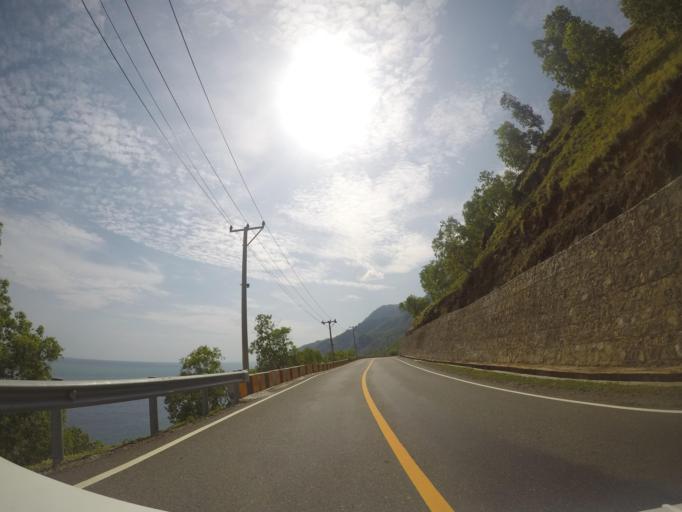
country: TL
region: Manatuto
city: Manatuto
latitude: -8.4761
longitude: 125.9051
